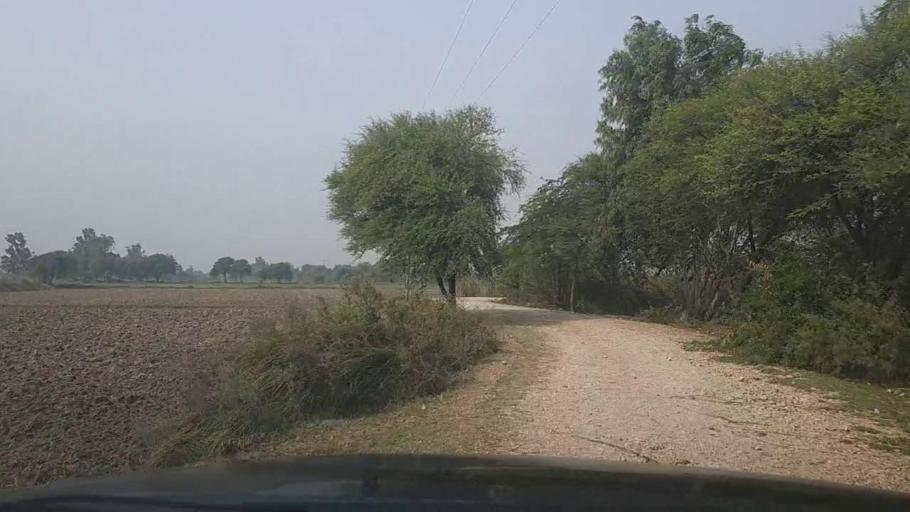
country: PK
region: Sindh
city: Mirpur Sakro
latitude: 24.5278
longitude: 67.8015
